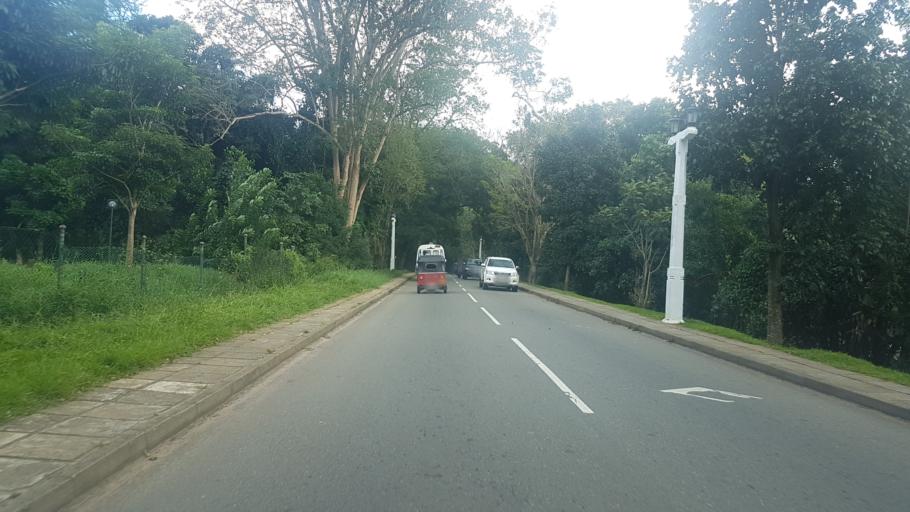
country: LK
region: Central
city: Kandy
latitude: 7.2638
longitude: 80.5974
